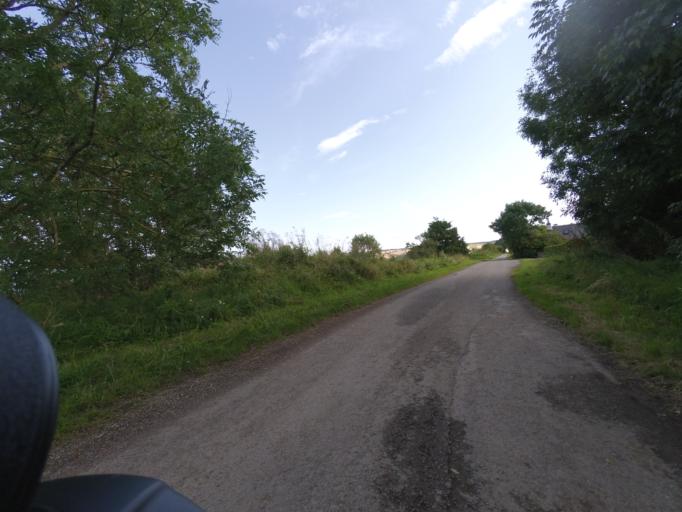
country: GB
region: Scotland
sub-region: Highland
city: Invergordon
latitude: 57.6755
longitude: -4.1656
